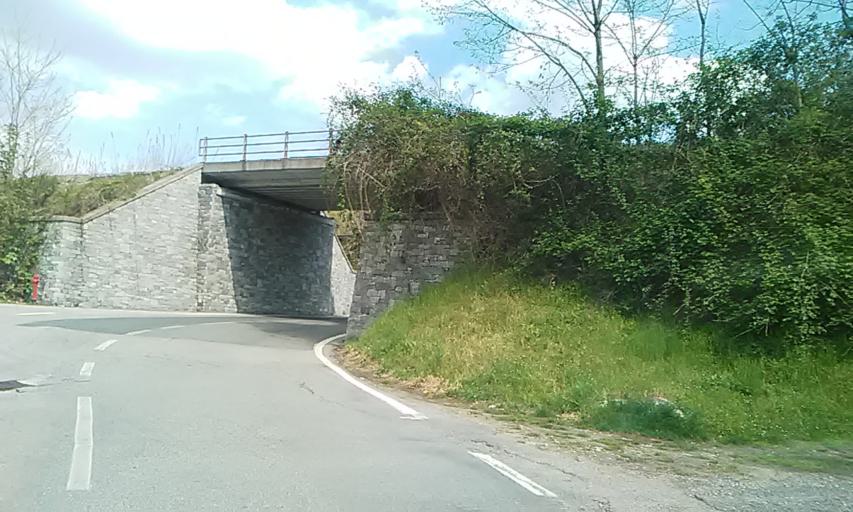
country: IT
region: Piedmont
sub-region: Provincia di Vercelli
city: Quarona
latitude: 45.7546
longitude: 8.2645
